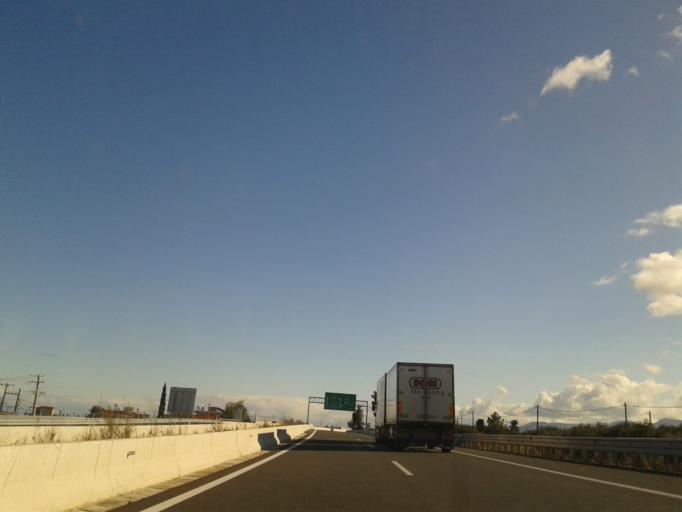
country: GR
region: West Greece
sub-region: Nomos Achaias
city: Selianitika
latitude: 38.2697
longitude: 22.0458
